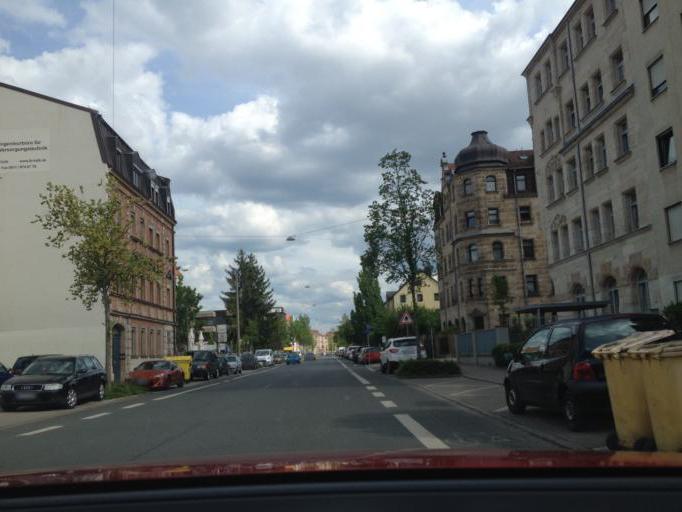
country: DE
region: Bavaria
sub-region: Regierungsbezirk Mittelfranken
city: Furth
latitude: 49.4638
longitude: 11.0042
